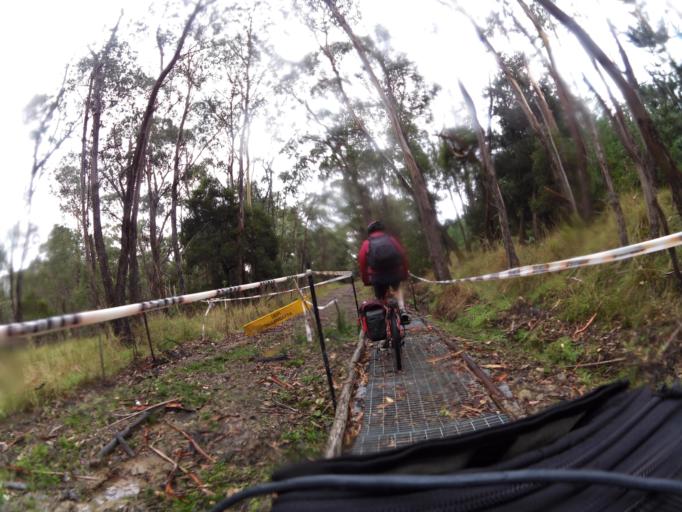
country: AU
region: New South Wales
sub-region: Greater Hume Shire
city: Holbrook
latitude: -36.1866
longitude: 147.5028
